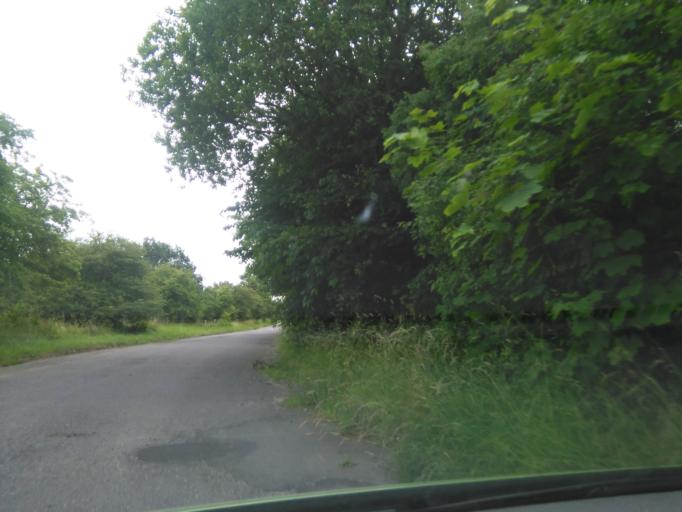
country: DK
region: Central Jutland
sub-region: Horsens Kommune
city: Horsens
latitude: 55.8743
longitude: 9.8864
